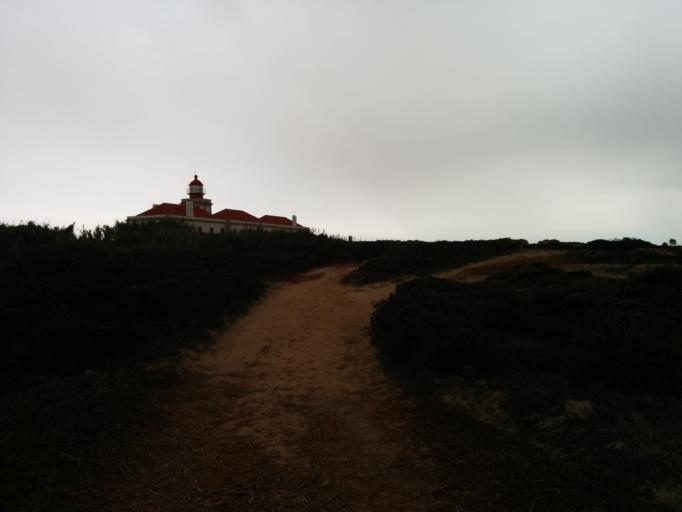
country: PT
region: Beja
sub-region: Odemira
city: Vila Nova de Milfontes
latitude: 37.5997
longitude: -8.8171
